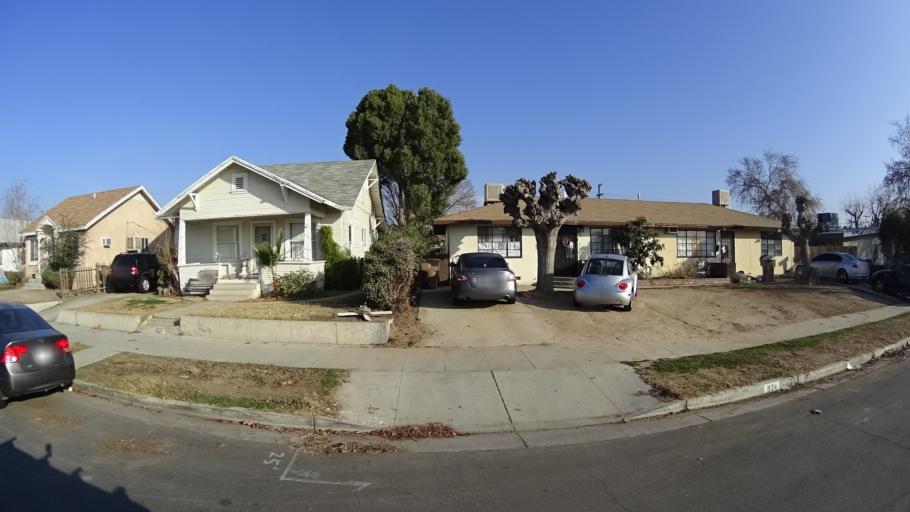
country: US
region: California
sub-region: Kern County
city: Bakersfield
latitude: 35.3832
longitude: -118.9861
